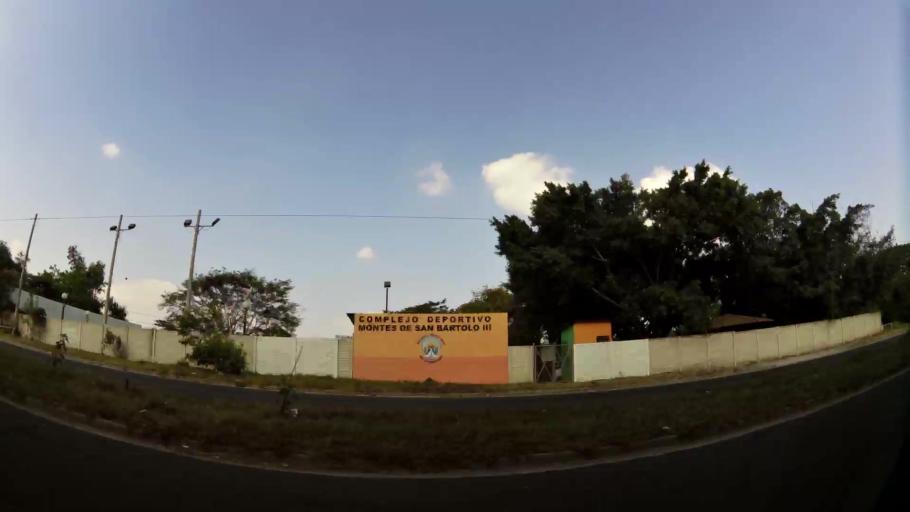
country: SV
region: San Salvador
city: Soyapango
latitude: 13.7178
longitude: -89.1311
